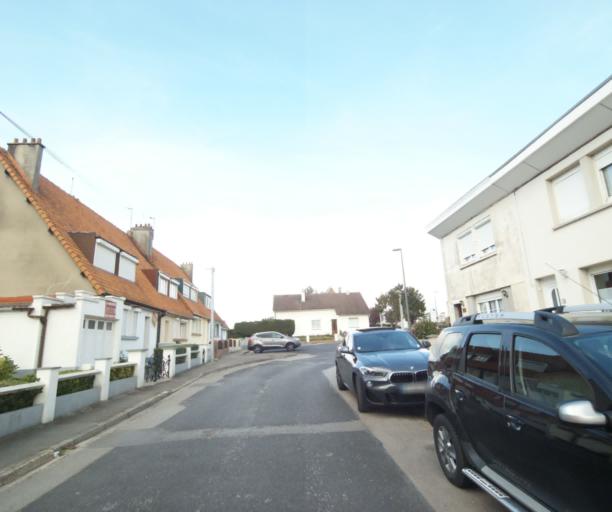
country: FR
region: Nord-Pas-de-Calais
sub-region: Departement du Pas-de-Calais
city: Etaples
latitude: 50.5232
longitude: 1.6270
